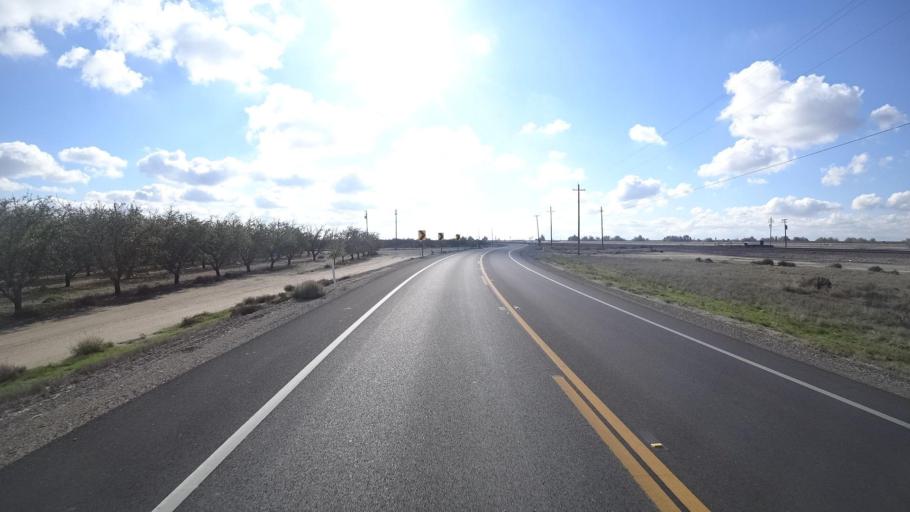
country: US
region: California
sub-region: Kern County
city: Wasco
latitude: 35.6748
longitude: -119.3302
